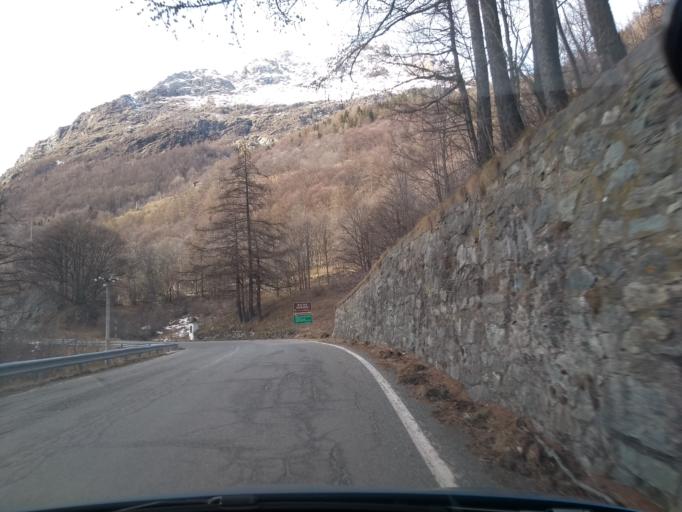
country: IT
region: Piedmont
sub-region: Provincia di Torino
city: Balme
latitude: 45.3097
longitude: 7.2481
